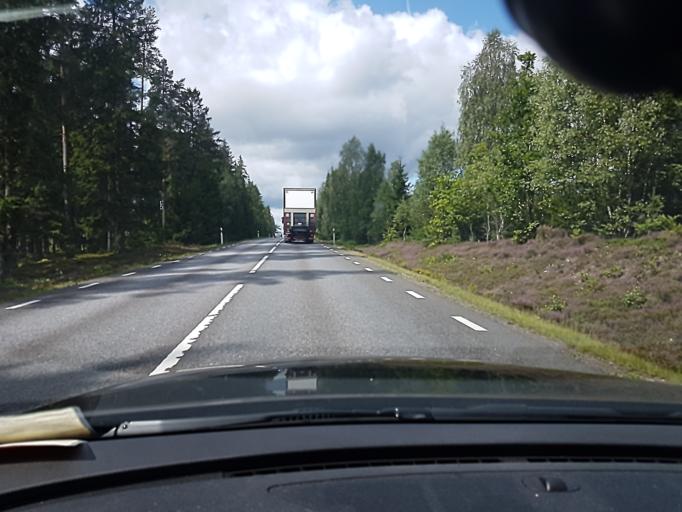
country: SE
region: Kronoberg
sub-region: Lessebo Kommun
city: Lessebo
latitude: 56.7321
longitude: 15.4174
